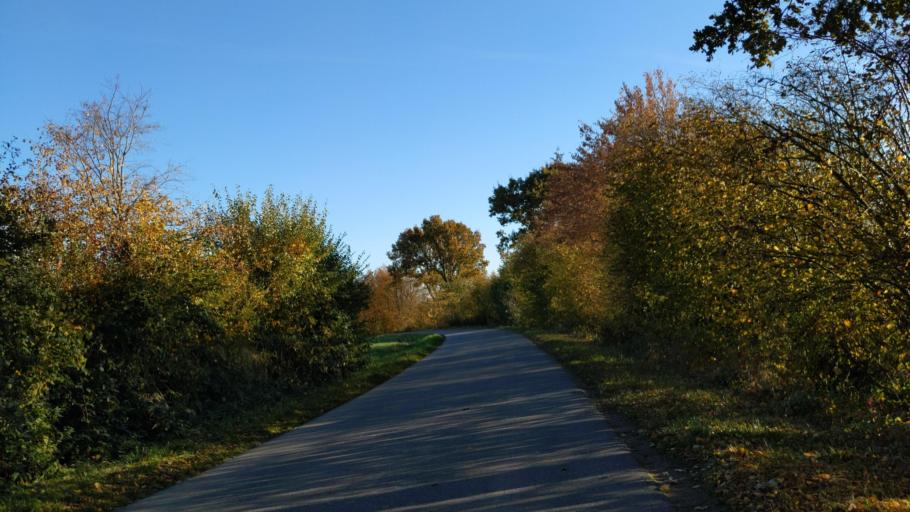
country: DE
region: Schleswig-Holstein
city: Einhaus
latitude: 53.7247
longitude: 10.7196
